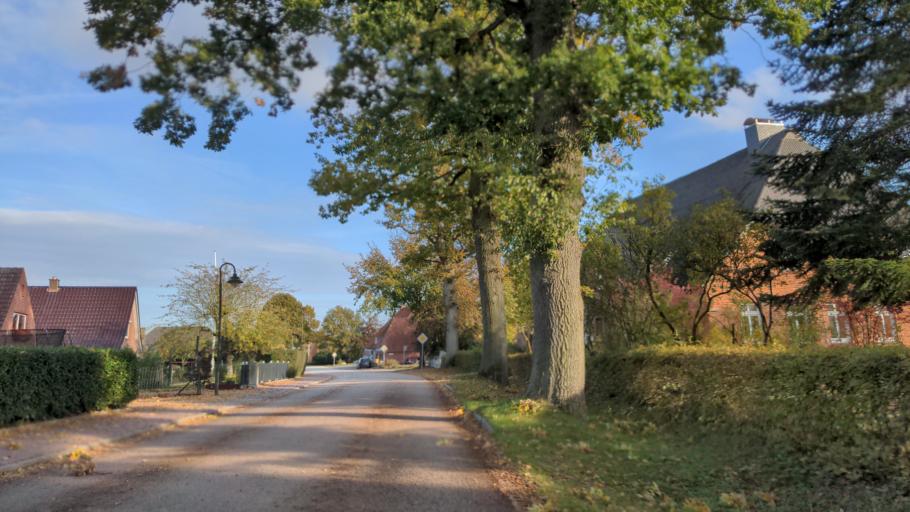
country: DE
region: Schleswig-Holstein
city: Damlos
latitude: 54.2432
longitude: 10.9063
